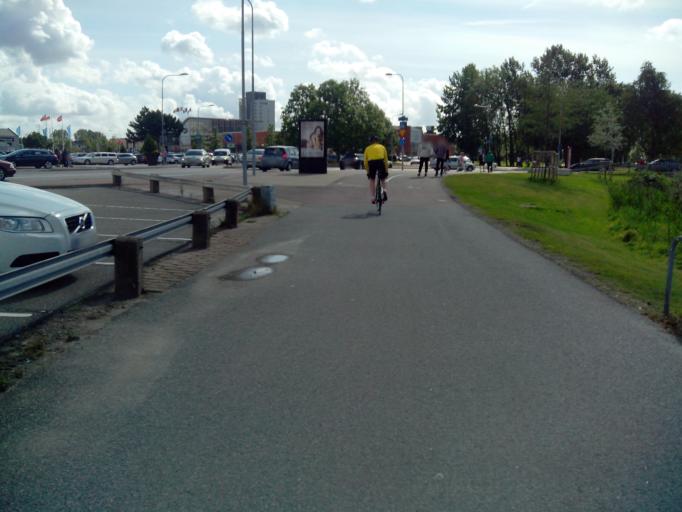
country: SE
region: Vaestra Goetaland
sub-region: Goteborg
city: Goeteborg
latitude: 57.7244
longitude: 11.9510
